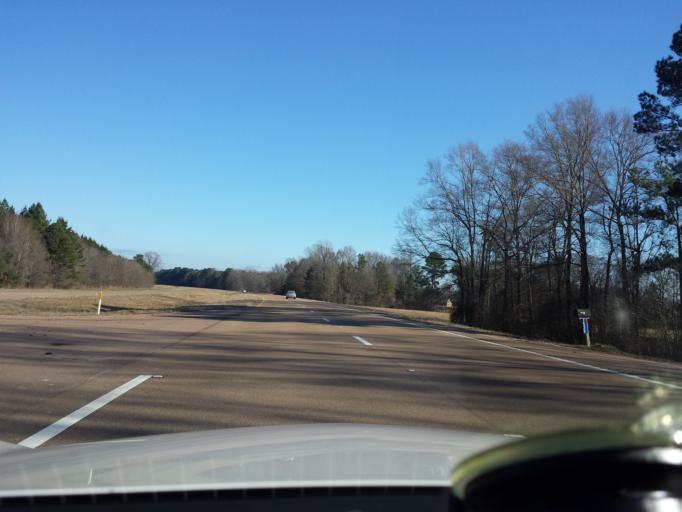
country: US
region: Mississippi
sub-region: Scott County
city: Morton
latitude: 32.5604
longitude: -89.7496
